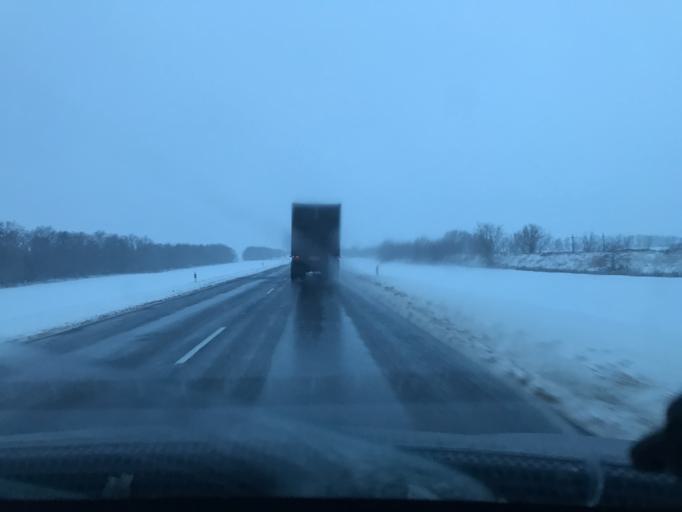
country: RU
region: Rostov
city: Letnik
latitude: 46.0386
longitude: 41.2110
